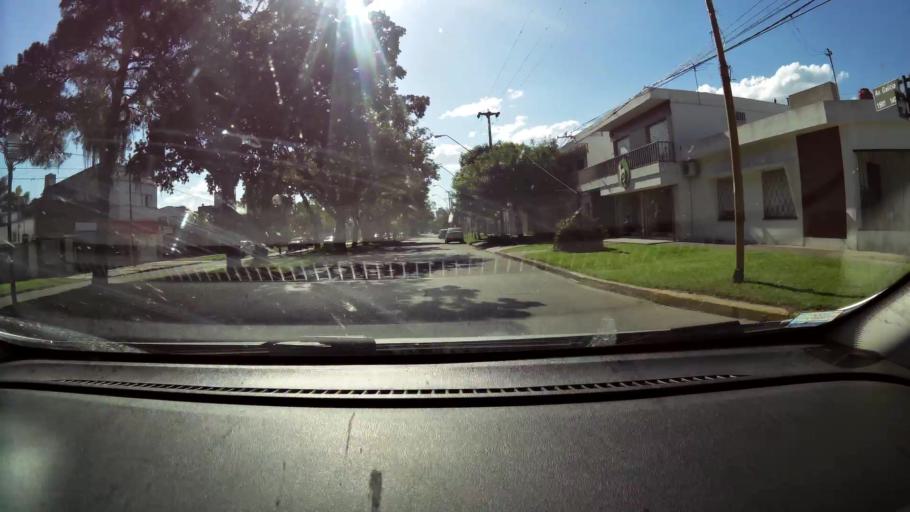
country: AR
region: Santa Fe
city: Santa Fe de la Vera Cruz
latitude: -31.6076
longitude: -60.6812
